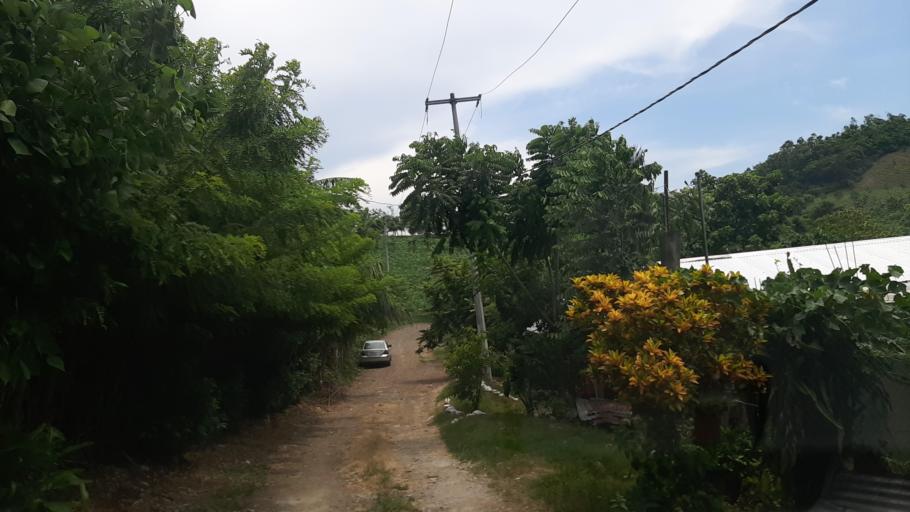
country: MX
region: Veracruz
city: Cazones de Herrera
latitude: 20.6797
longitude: -97.3233
